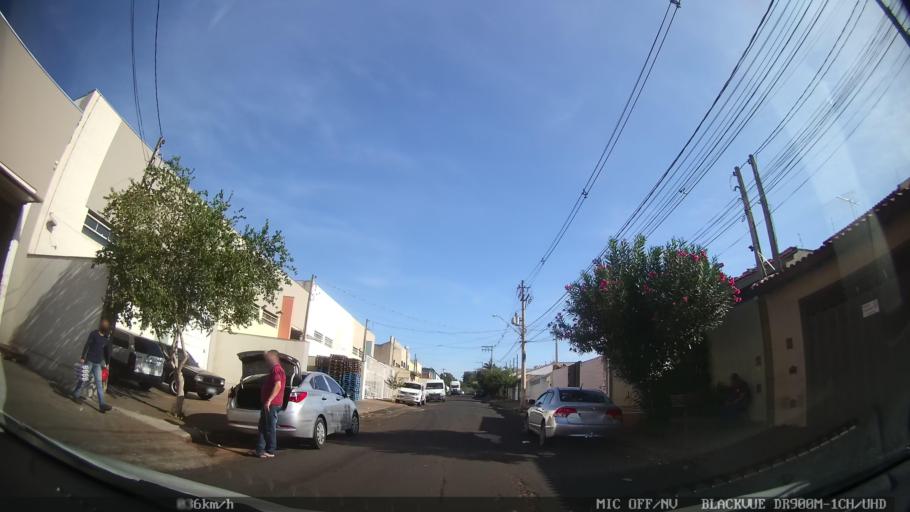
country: BR
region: Sao Paulo
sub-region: Ribeirao Preto
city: Ribeirao Preto
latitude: -21.1770
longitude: -47.7618
